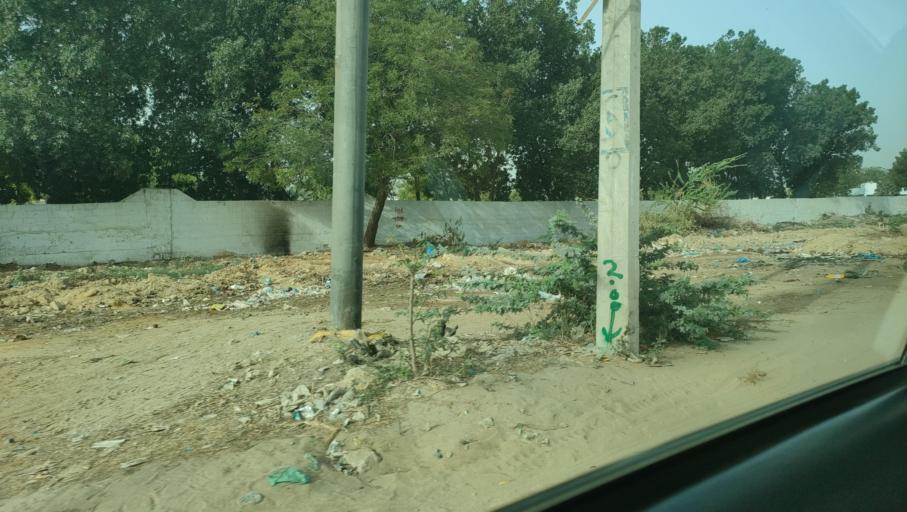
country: PK
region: Sindh
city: Malir Cantonment
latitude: 24.9354
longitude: 67.1702
